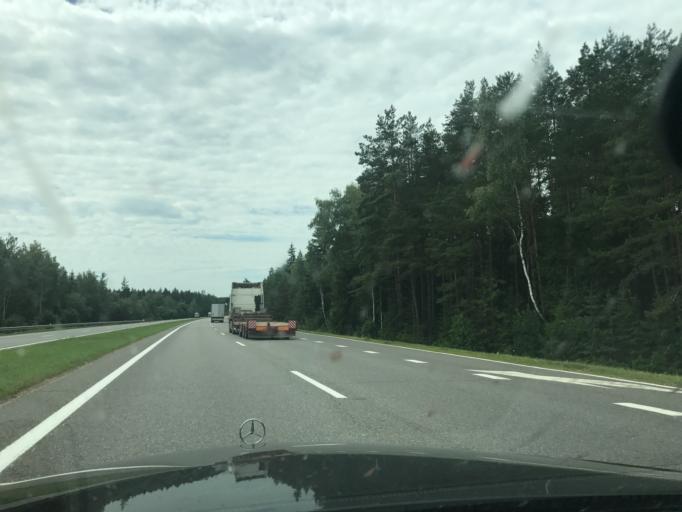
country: BY
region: Minsk
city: Zamostochcha
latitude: 53.8757
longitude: 27.9290
